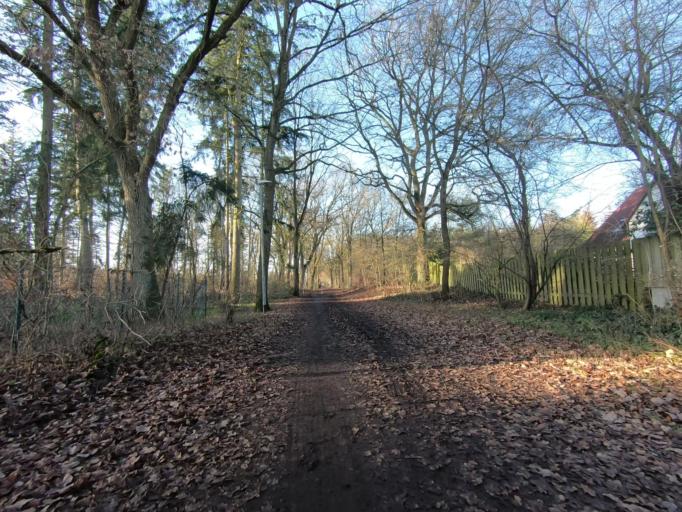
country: DE
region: Lower Saxony
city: Gifhorn
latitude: 52.4634
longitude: 10.5671
